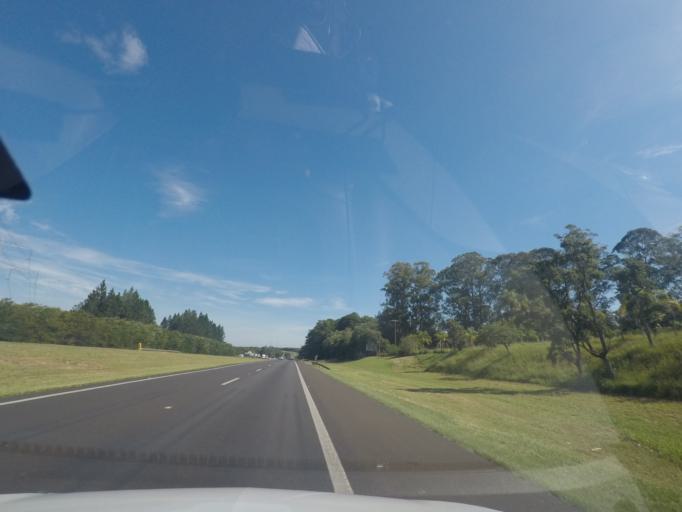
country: BR
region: Sao Paulo
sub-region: Itirapina
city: Itirapina
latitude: -22.1556
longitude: -47.7933
